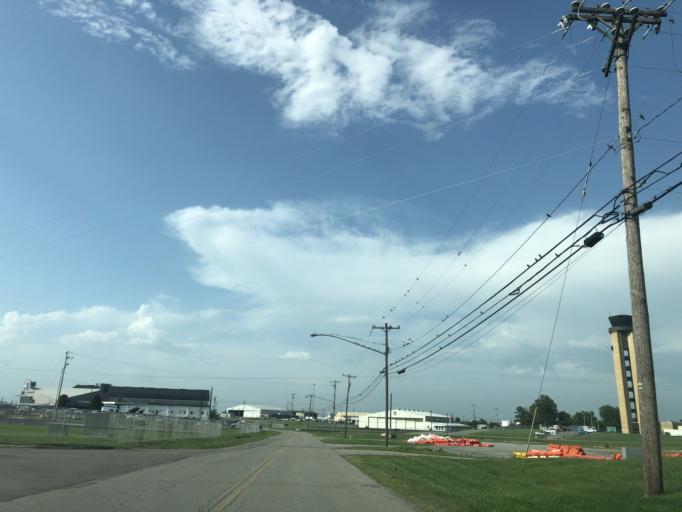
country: US
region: Tennessee
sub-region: Davidson County
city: Oak Hill
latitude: 36.1147
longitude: -86.6778
